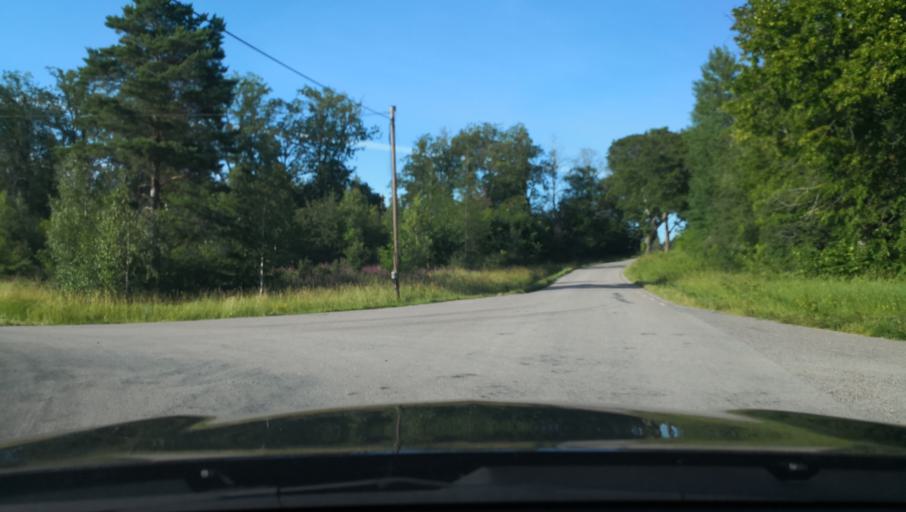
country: SE
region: Uppsala
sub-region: Uppsala Kommun
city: Vattholma
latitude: 59.9169
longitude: 17.8430
